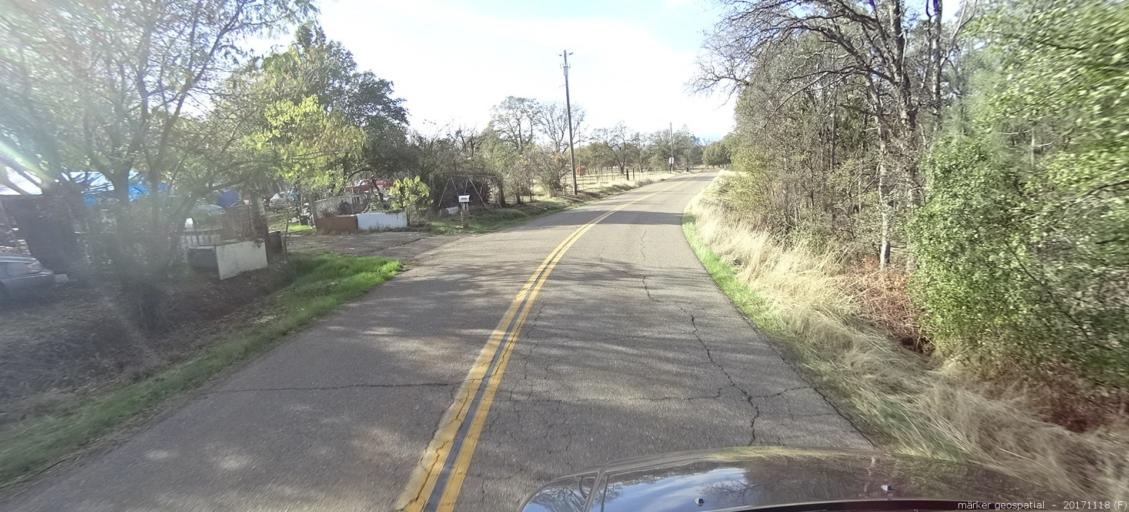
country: US
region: California
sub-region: Shasta County
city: Redding
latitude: 40.4720
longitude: -122.4194
